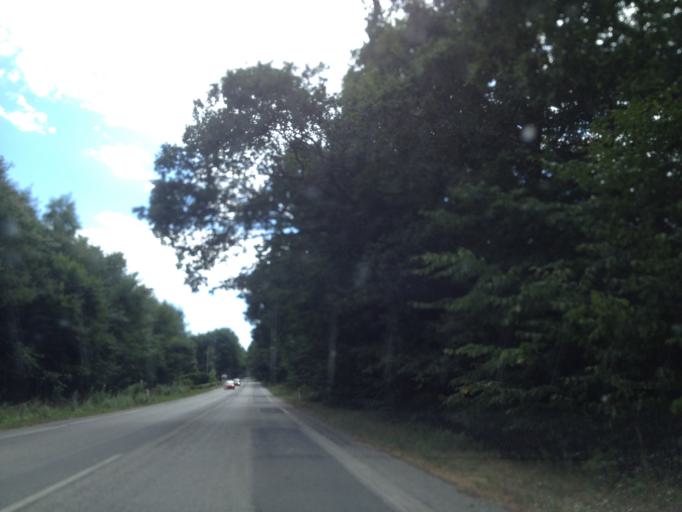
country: DK
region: Zealand
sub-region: Guldborgsund Kommune
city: Sakskobing
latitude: 54.7843
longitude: 11.6445
